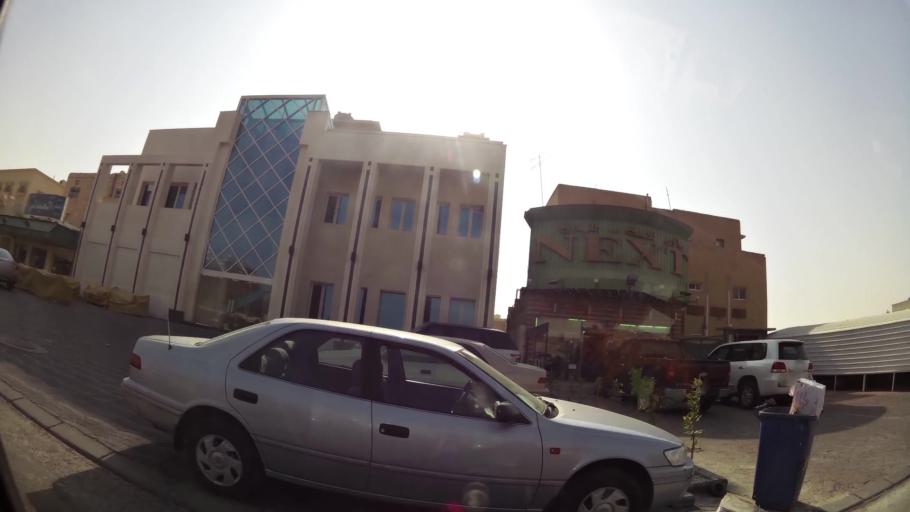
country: KW
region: Muhafazat al Jahra'
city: Al Jahra'
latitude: 29.3576
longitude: 47.6746
